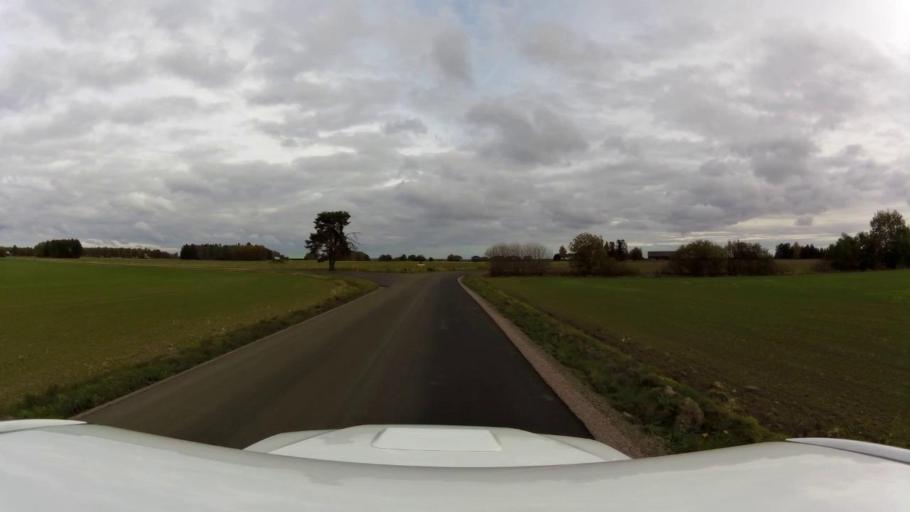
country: SE
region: OEstergoetland
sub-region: Linkopings Kommun
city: Linkoping
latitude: 58.4425
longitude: 15.5797
